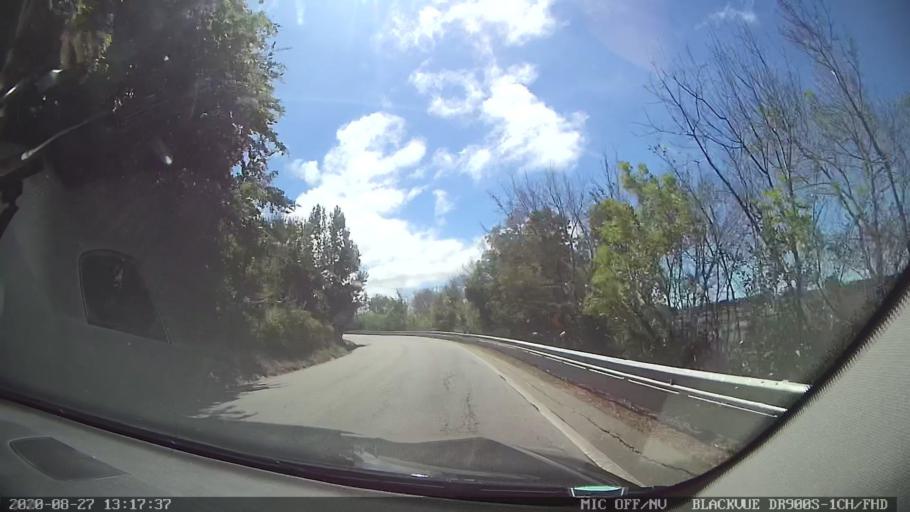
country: PT
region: Aveiro
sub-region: Ilhavo
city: Ilhavo
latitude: 40.5808
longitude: -8.6814
